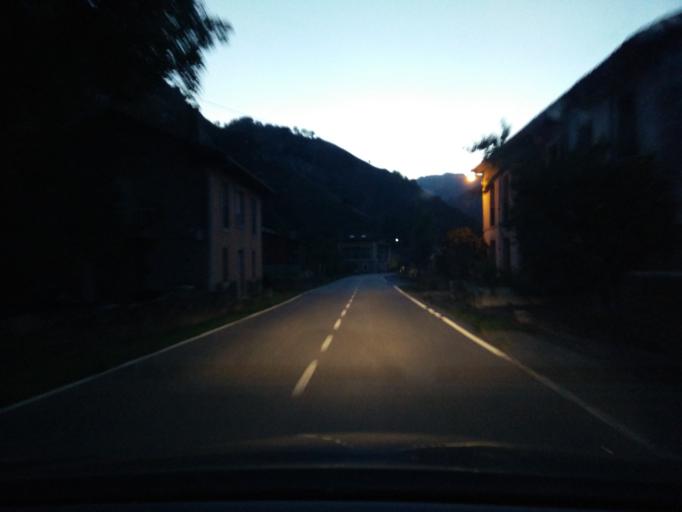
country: ES
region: Asturias
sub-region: Province of Asturias
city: Amieva
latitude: 43.2689
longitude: -5.1370
